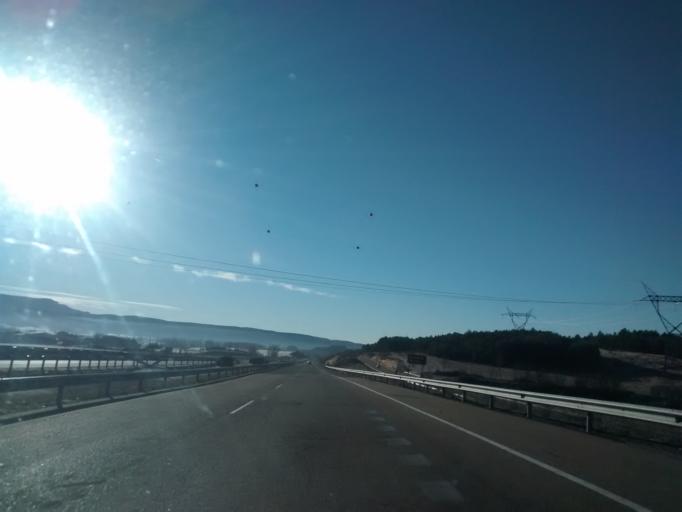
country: ES
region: Castille and Leon
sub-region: Provincia de Palencia
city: Aguilar de Campoo
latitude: 42.7495
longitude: -4.2931
